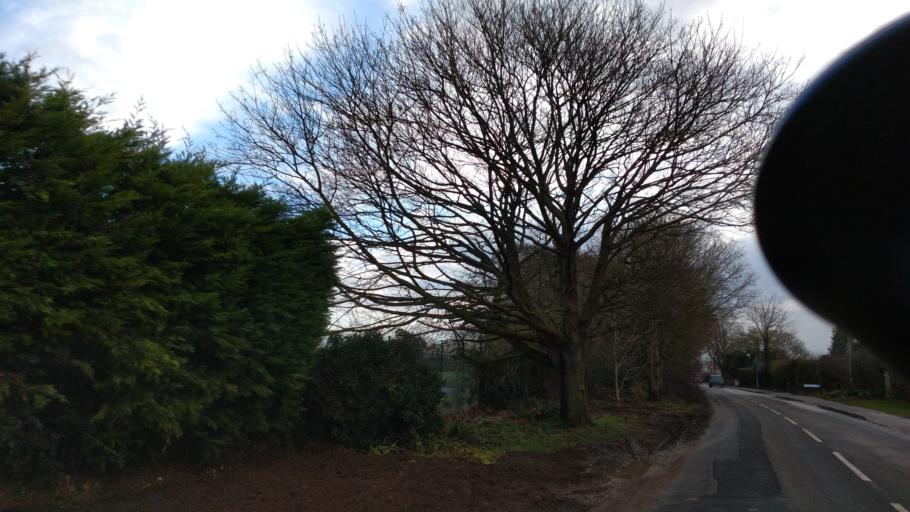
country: GB
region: England
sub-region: Borough of Swindon
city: Highworth
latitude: 51.6259
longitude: -1.7098
